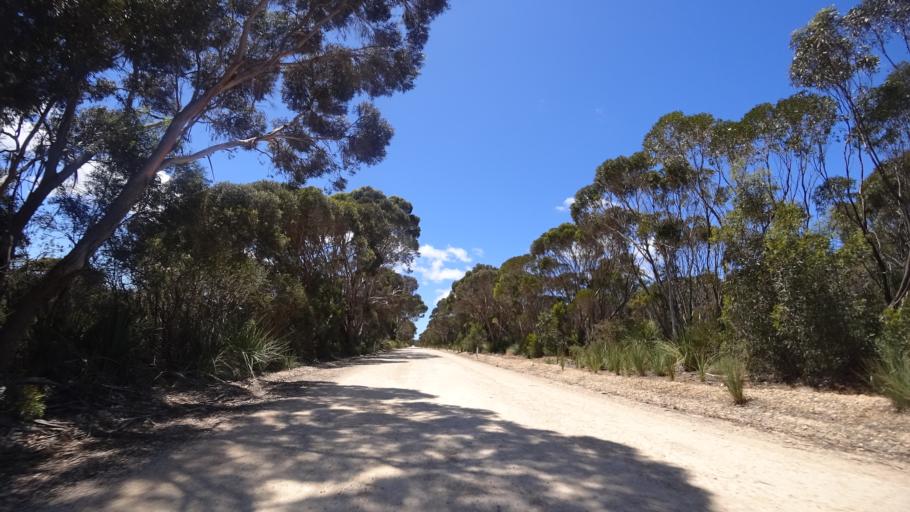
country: AU
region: South Australia
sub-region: Kangaroo Island
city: Kingscote
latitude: -35.8264
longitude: 138.0054
